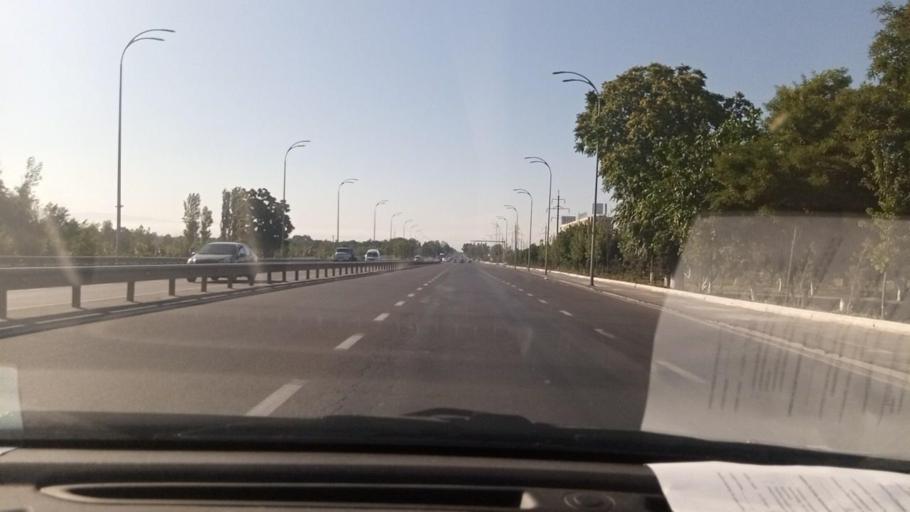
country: UZ
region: Toshkent Shahri
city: Bektemir
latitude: 41.2596
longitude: 69.3770
